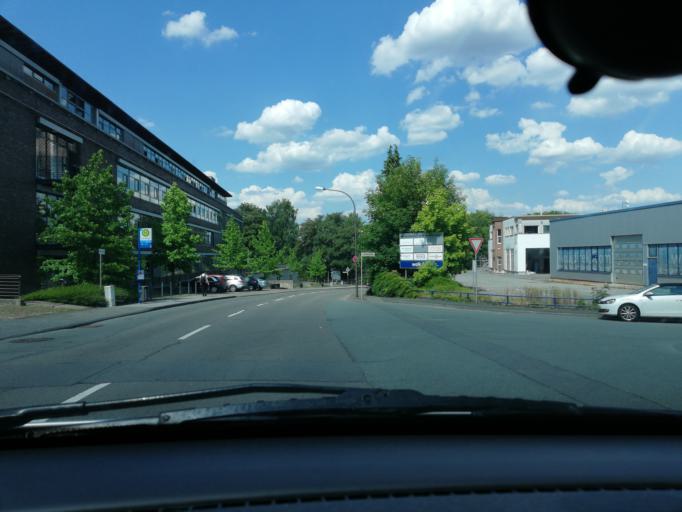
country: DE
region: North Rhine-Westphalia
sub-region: Regierungsbezirk Dusseldorf
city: Wuppertal
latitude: 51.2436
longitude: 7.1288
